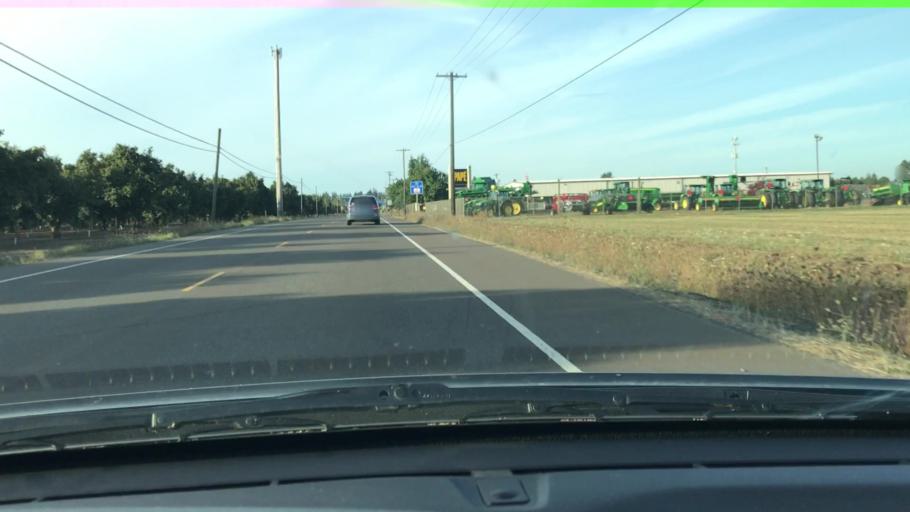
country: US
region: Oregon
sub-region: Yamhill County
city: McMinnville
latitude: 45.1861
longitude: -123.2100
